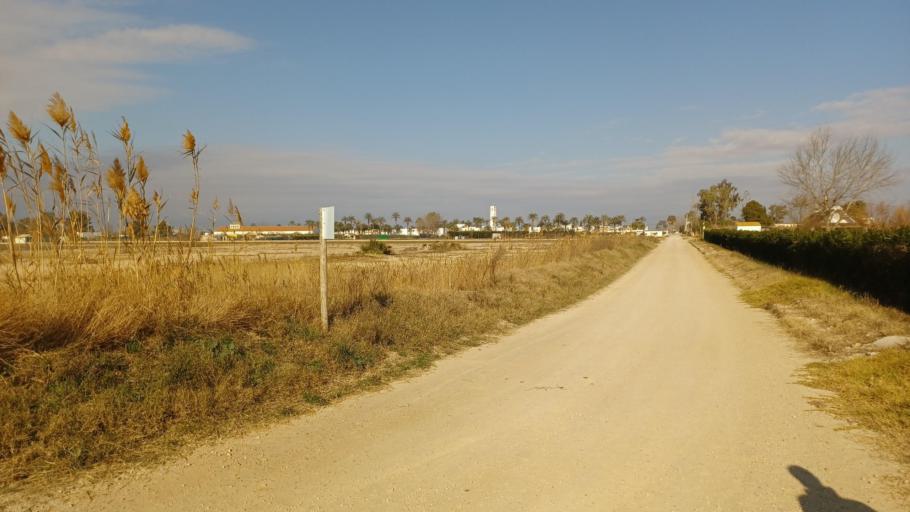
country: ES
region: Catalonia
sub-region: Provincia de Tarragona
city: Deltebre
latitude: 40.6413
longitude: 0.6903
